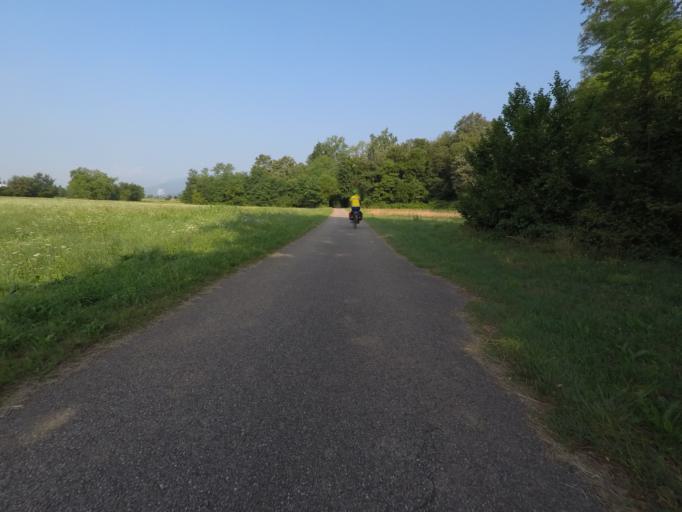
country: IT
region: Friuli Venezia Giulia
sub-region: Provincia di Pordenone
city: Travesio
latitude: 46.2003
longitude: 12.8483
